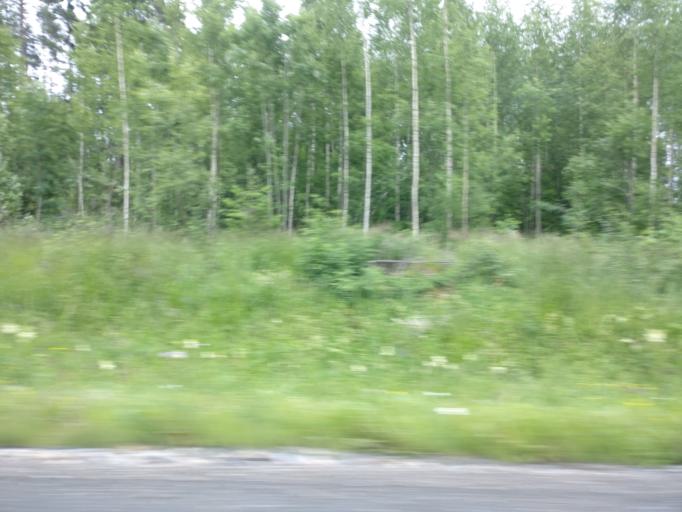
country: FI
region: Northern Savo
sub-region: Varkaus
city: Leppaevirta
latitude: 62.6092
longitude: 27.6232
